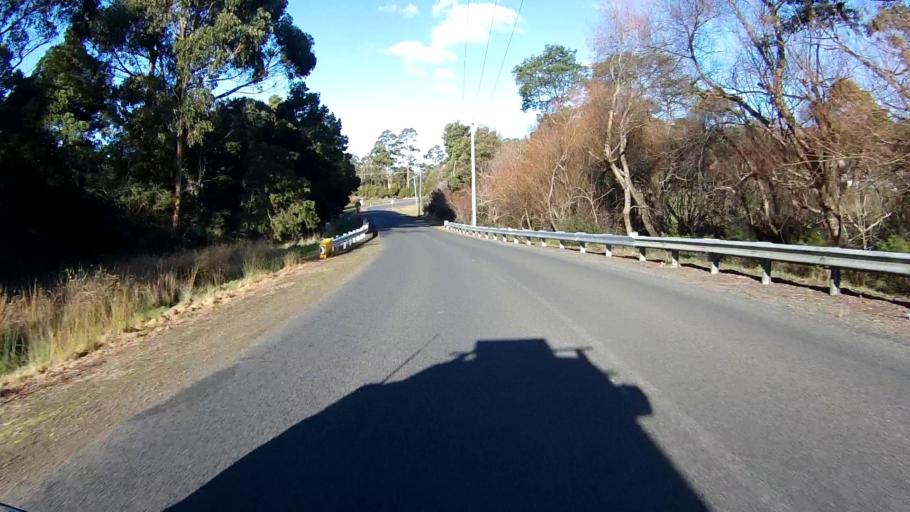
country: AU
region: Tasmania
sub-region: Clarence
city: Sandford
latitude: -43.1503
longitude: 147.8438
